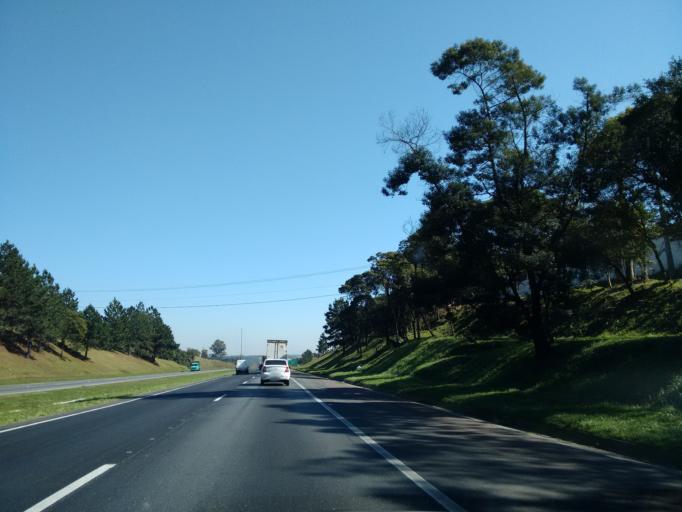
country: BR
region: Parana
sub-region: Sao Jose Dos Pinhais
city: Sao Jose dos Pinhais
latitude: -25.5710
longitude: -49.2110
